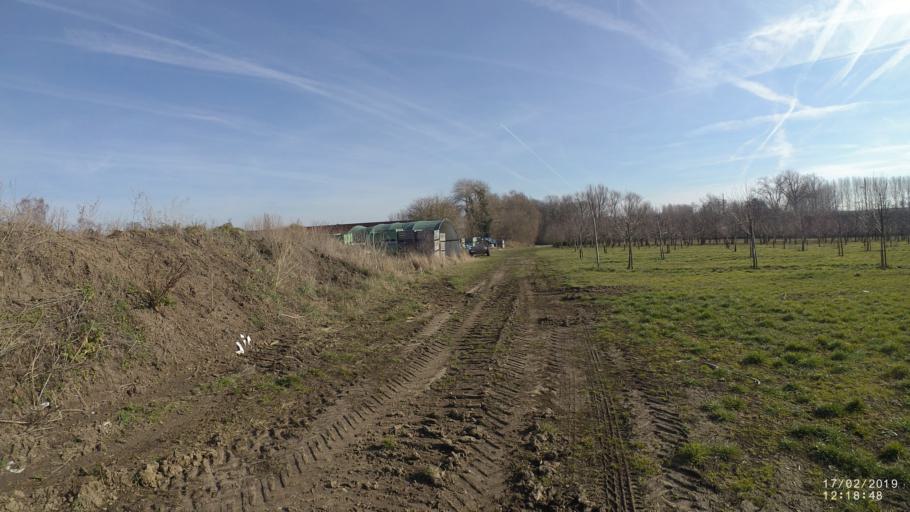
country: BE
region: Flanders
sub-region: Provincie Limburg
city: Sint-Truiden
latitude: 50.8111
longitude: 5.1528
